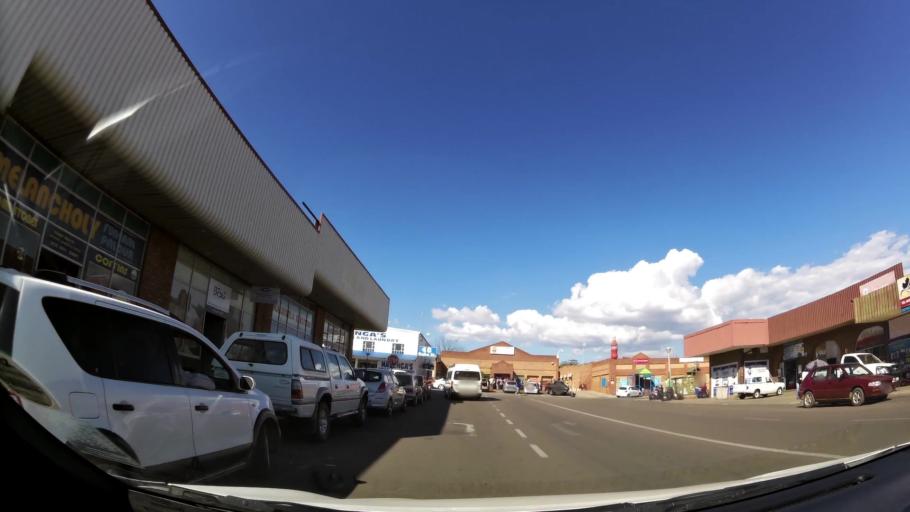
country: ZA
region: Limpopo
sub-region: Waterberg District Municipality
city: Mokopane
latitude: -24.1821
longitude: 29.0175
